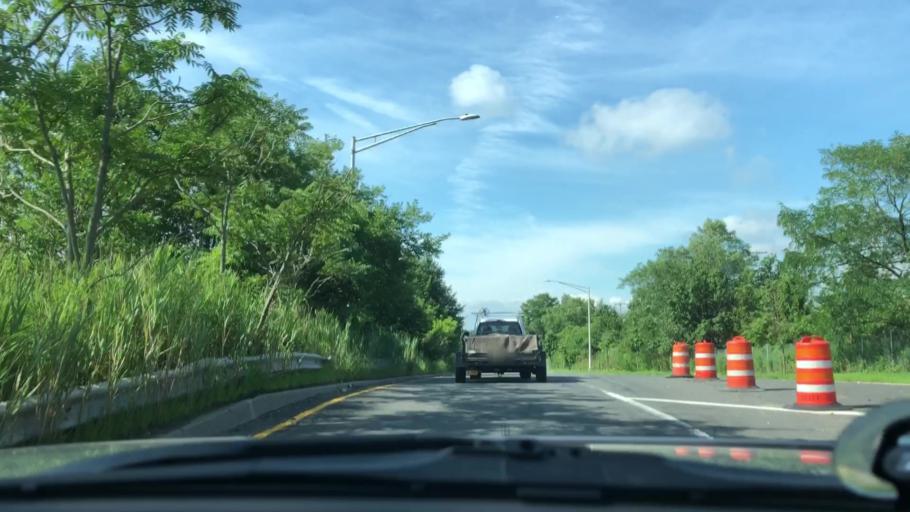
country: US
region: New Jersey
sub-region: Middlesex County
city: Carteret
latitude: 40.5701
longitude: -74.1912
